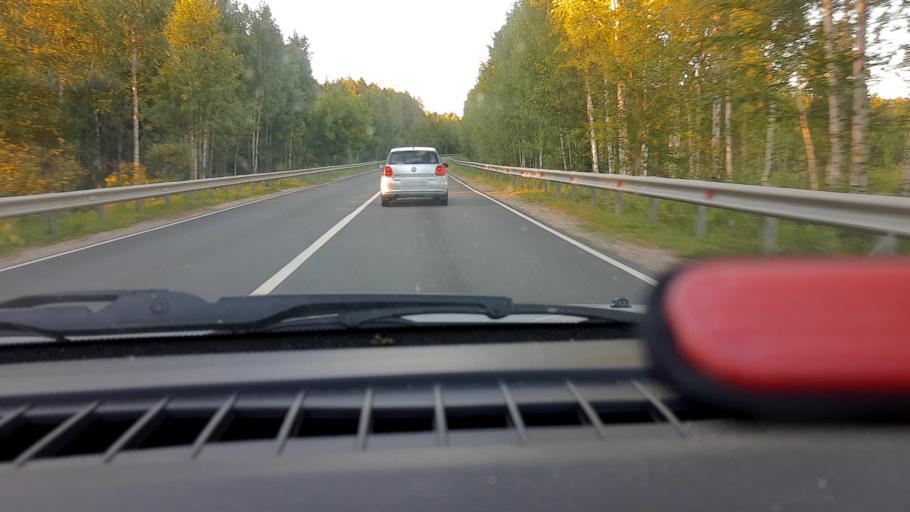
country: RU
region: Nizjnij Novgorod
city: Krasnyye Baki
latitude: 57.1337
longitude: 45.2150
